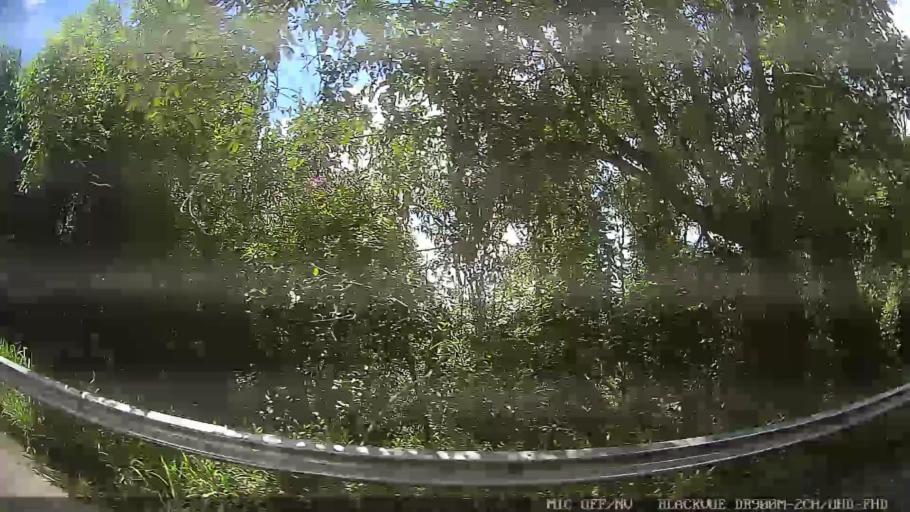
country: BR
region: Sao Paulo
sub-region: Amparo
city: Amparo
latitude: -22.8024
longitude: -46.7175
